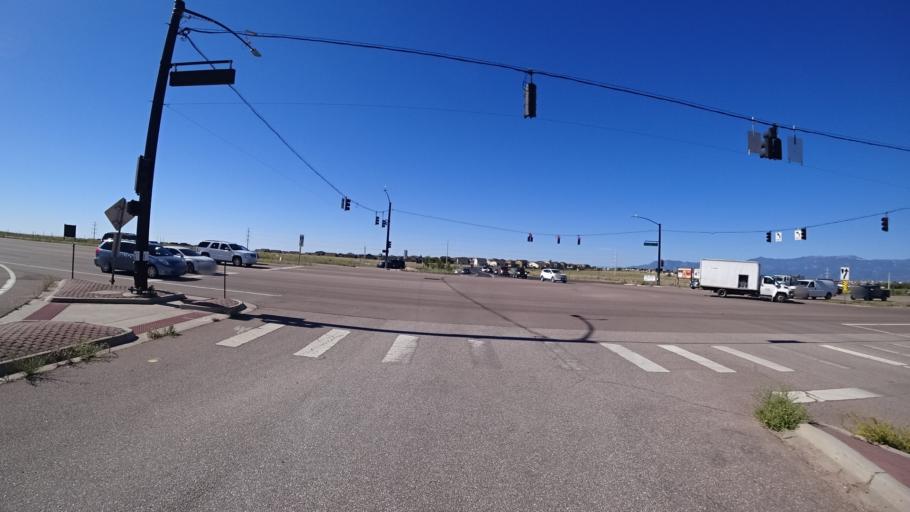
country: US
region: Colorado
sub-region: El Paso County
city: Black Forest
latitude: 38.9410
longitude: -104.6781
